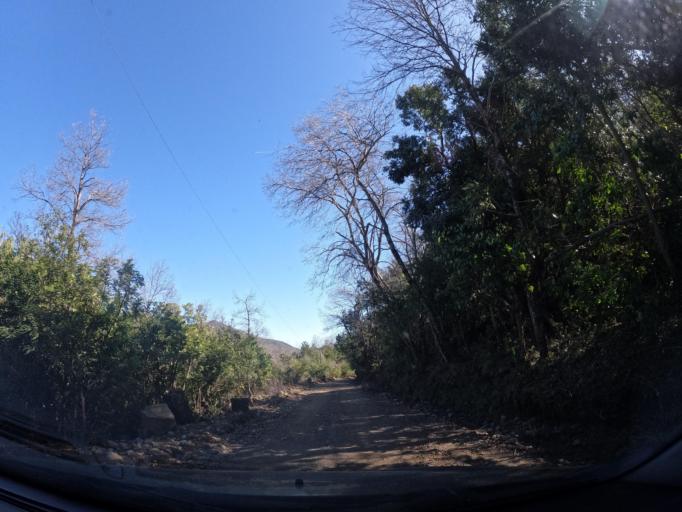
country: CL
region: Maule
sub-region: Provincia de Linares
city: Longavi
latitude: -36.2471
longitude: -71.3389
